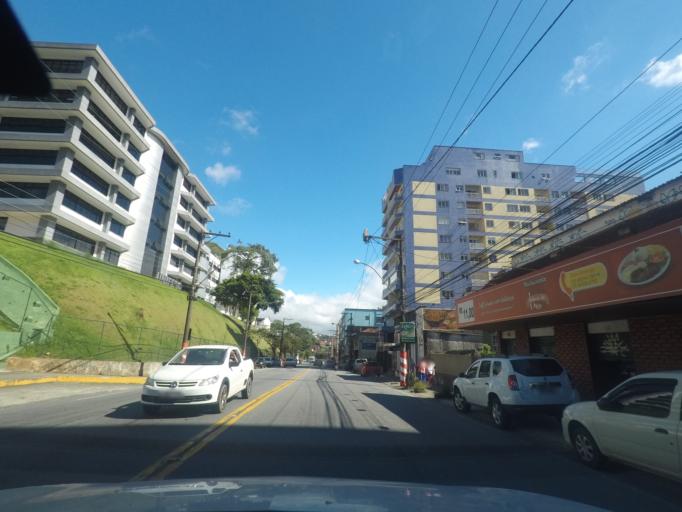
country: BR
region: Rio de Janeiro
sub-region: Teresopolis
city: Teresopolis
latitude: -22.4348
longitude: -42.9785
